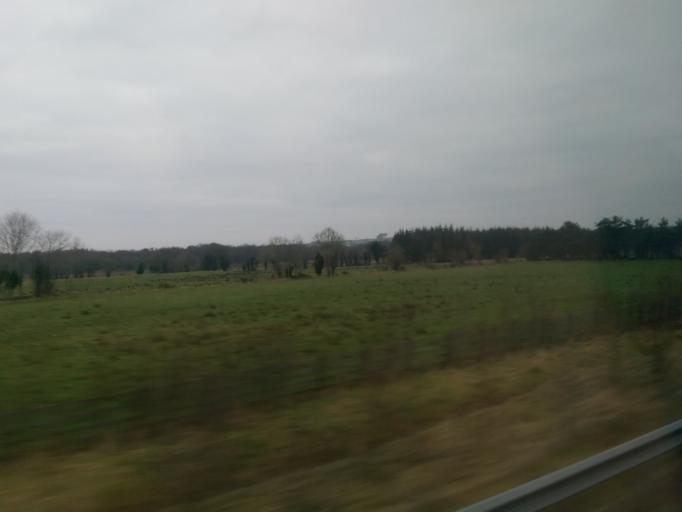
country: IE
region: Connaught
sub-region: County Galway
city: Ballinasloe
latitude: 53.3082
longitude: -8.3127
